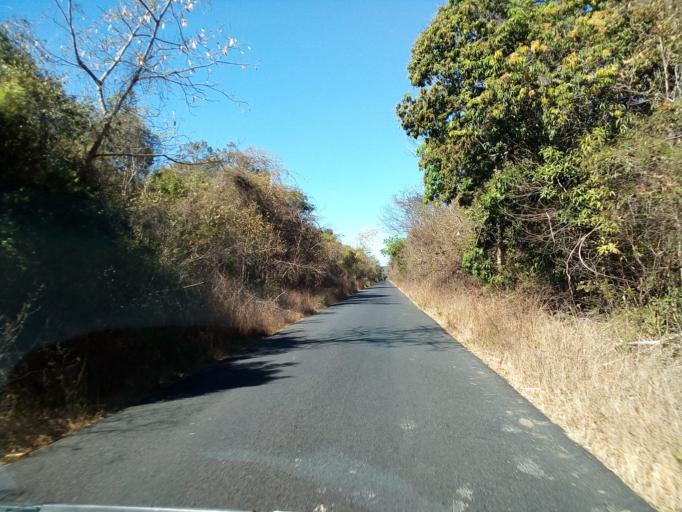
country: MG
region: Boeny
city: Ambato Boeny
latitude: -16.2875
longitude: 46.8111
